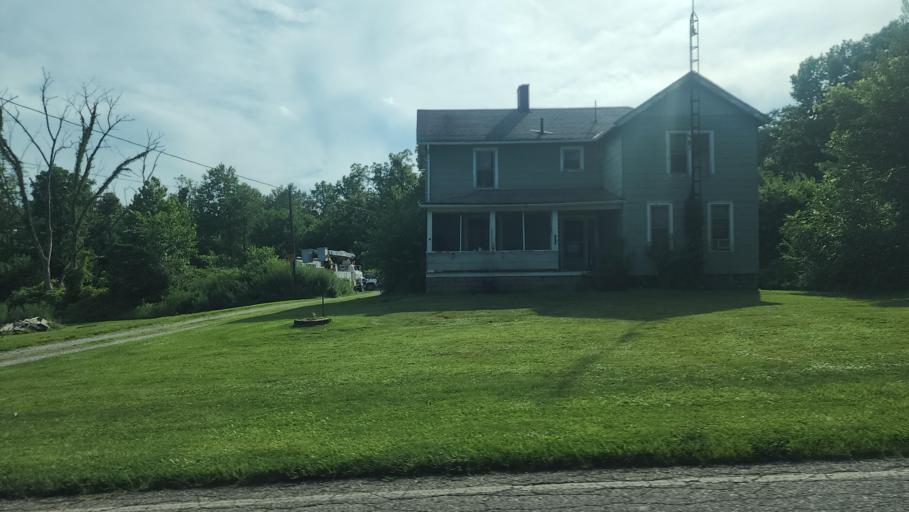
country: US
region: Ohio
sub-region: Trumbull County
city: Niles
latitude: 41.1623
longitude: -80.7772
